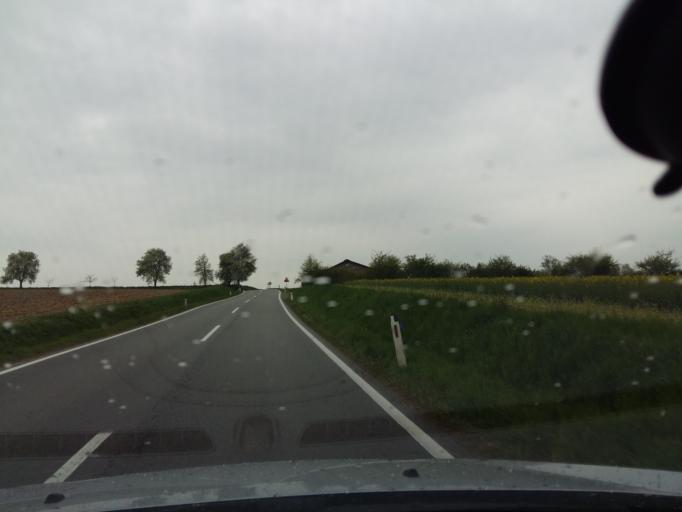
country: AT
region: Upper Austria
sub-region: Politischer Bezirk Scharding
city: Sankt Marienkirchen bei Schaerding
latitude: 48.4086
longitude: 13.5006
